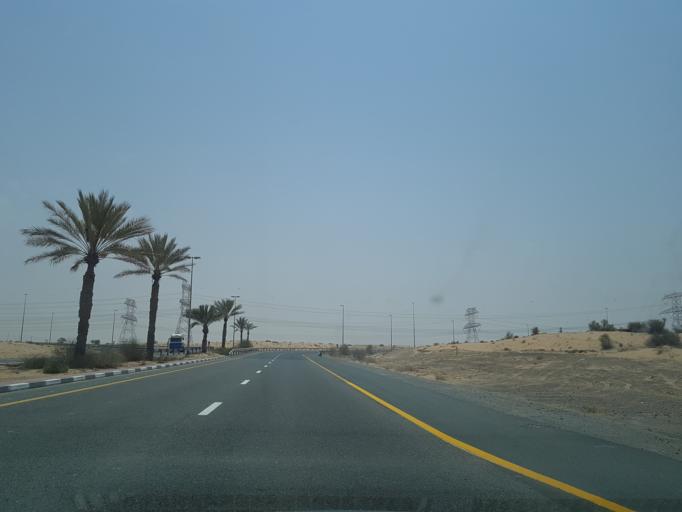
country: AE
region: Ash Shariqah
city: Sharjah
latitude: 25.1049
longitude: 55.4130
